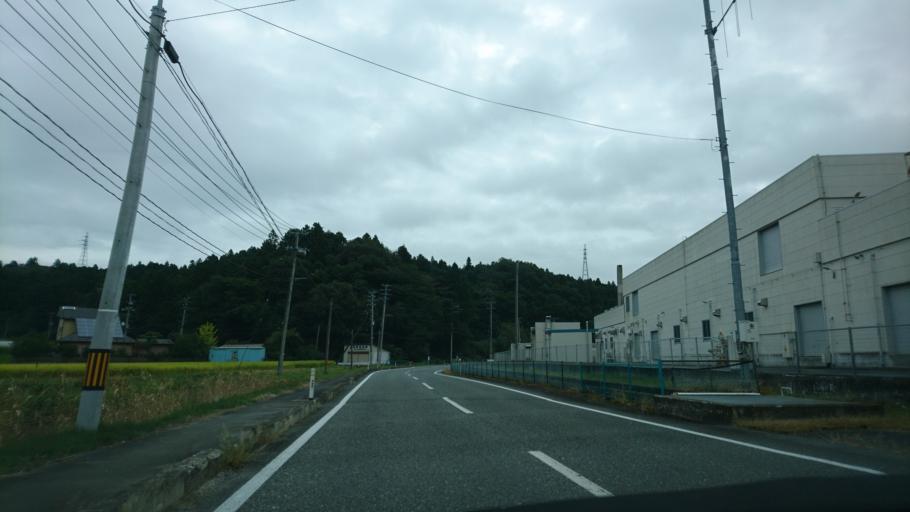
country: JP
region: Iwate
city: Ichinoseki
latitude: 38.8100
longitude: 141.0821
